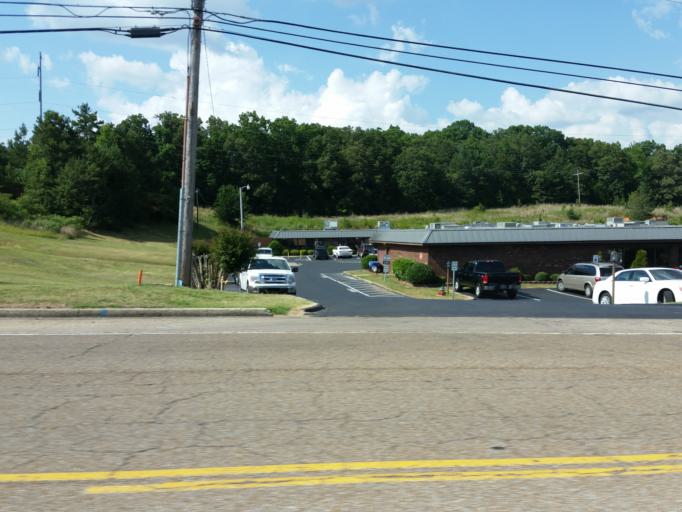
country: US
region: Tennessee
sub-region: Henderson County
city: Lexington
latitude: 35.6416
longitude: -88.3781
